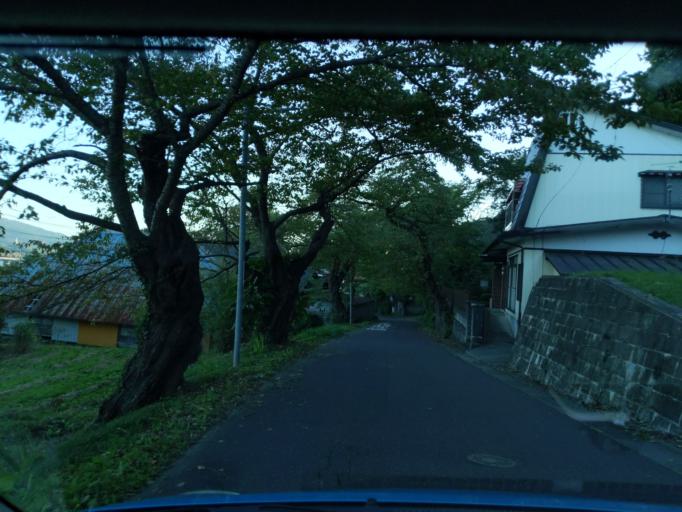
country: JP
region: Iwate
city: Mizusawa
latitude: 39.0481
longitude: 141.1208
